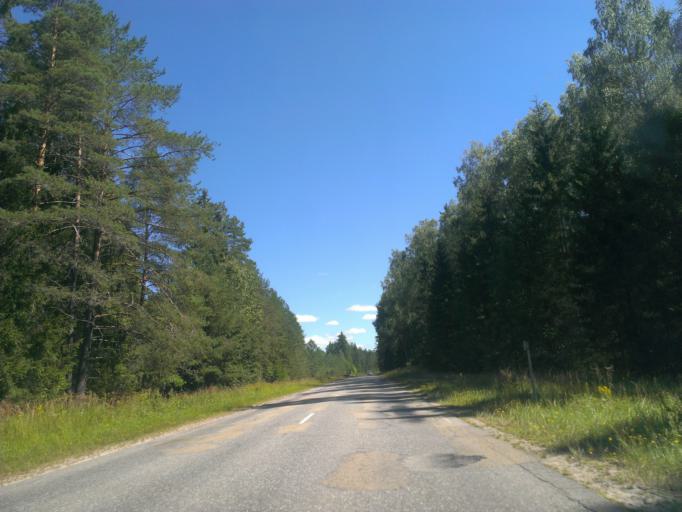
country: LV
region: Incukalns
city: Incukalns
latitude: 57.0320
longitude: 24.6909
